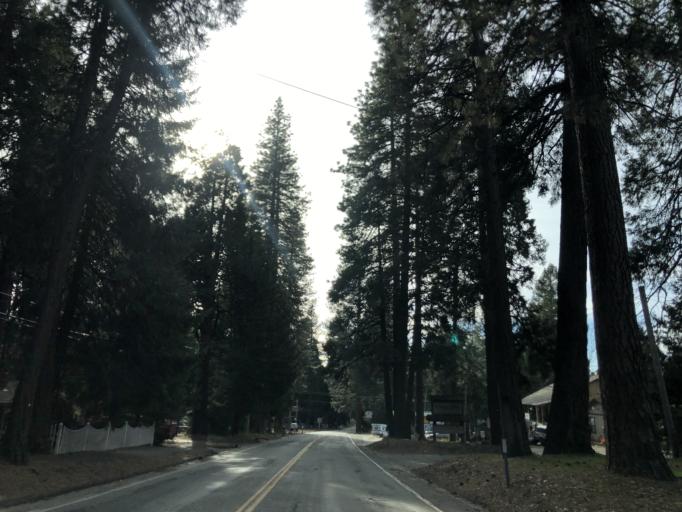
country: US
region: California
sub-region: El Dorado County
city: Pollock Pines
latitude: 38.7591
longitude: -120.5897
